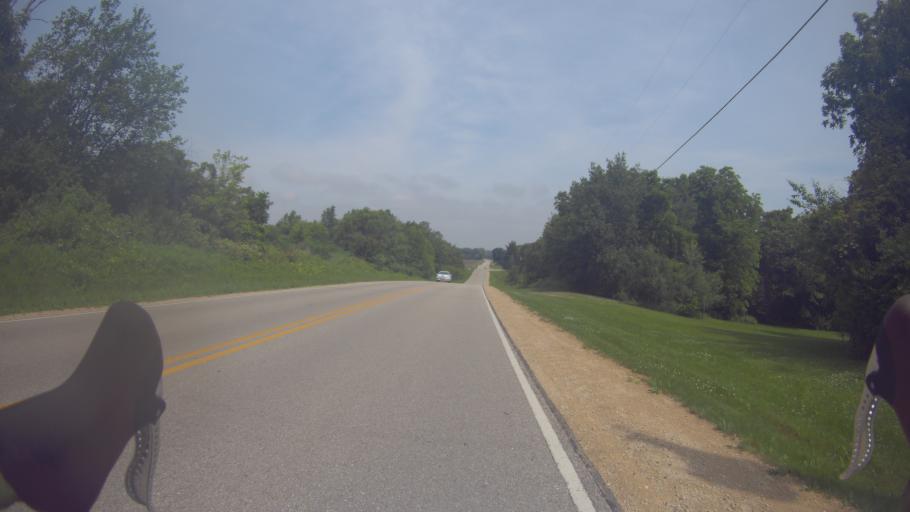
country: US
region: Wisconsin
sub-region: Rock County
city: Edgerton
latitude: 42.8594
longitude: -89.0292
